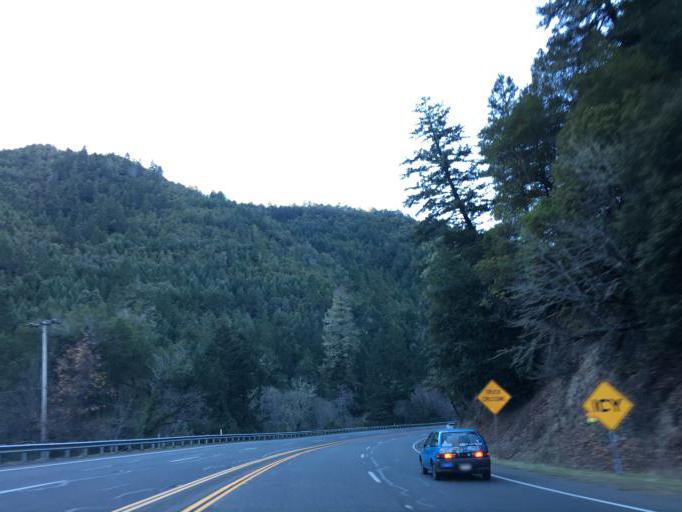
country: US
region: California
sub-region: Mendocino County
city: Brooktrails
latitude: 39.5352
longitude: -123.4103
